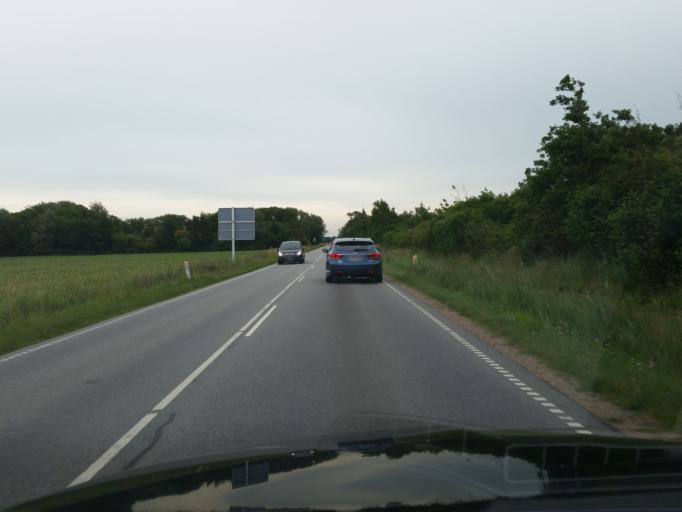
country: DK
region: South Denmark
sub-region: Varde Kommune
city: Oksbol
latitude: 55.7879
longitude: 8.2519
